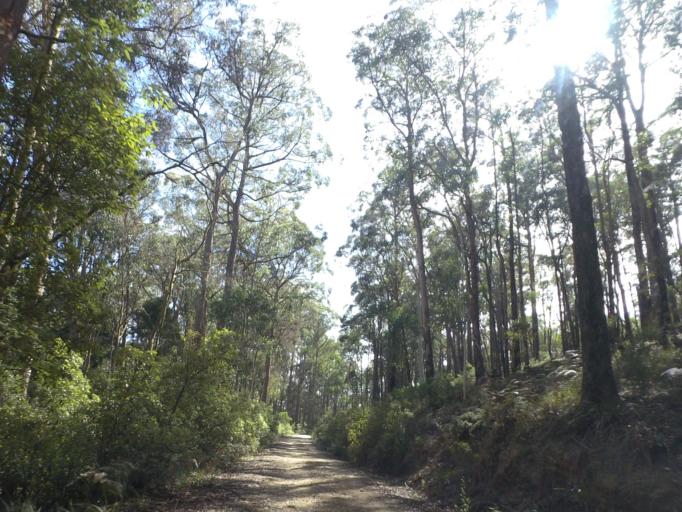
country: AU
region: Victoria
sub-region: Moorabool
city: Bacchus Marsh
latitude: -37.4476
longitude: 144.2623
